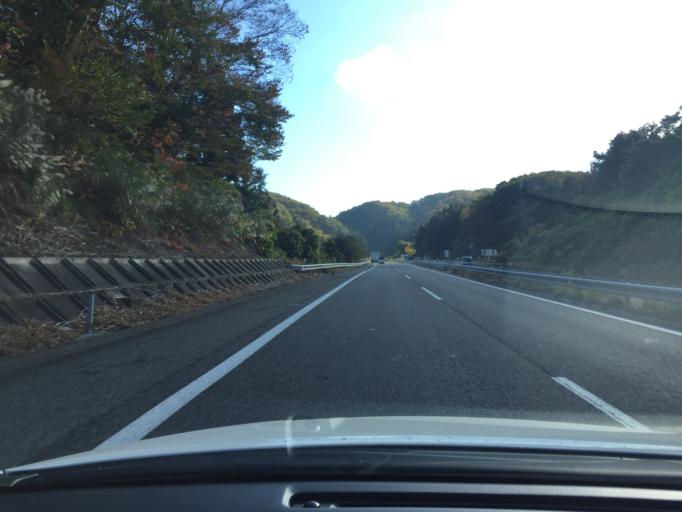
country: JP
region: Fukushima
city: Funehikimachi-funehiki
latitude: 37.3563
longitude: 140.6084
